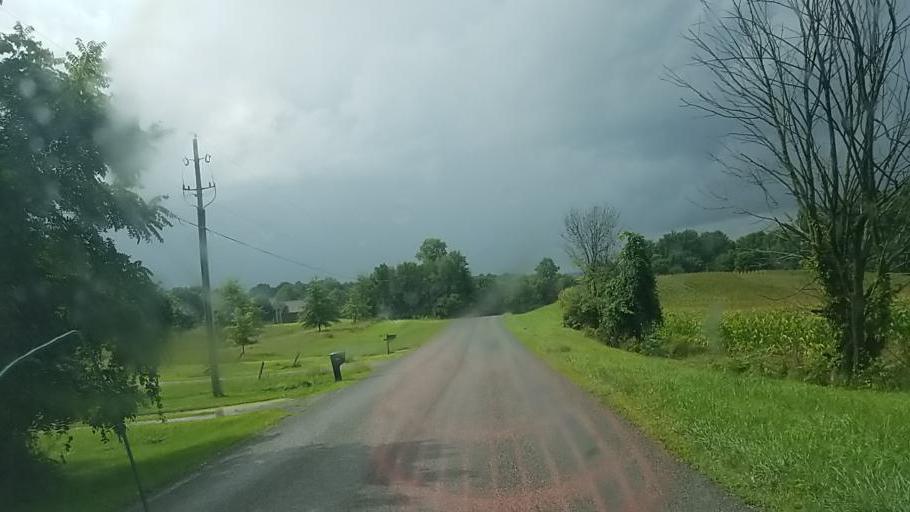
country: US
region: Ohio
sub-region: Champaign County
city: North Lewisburg
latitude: 40.3125
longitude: -83.6254
